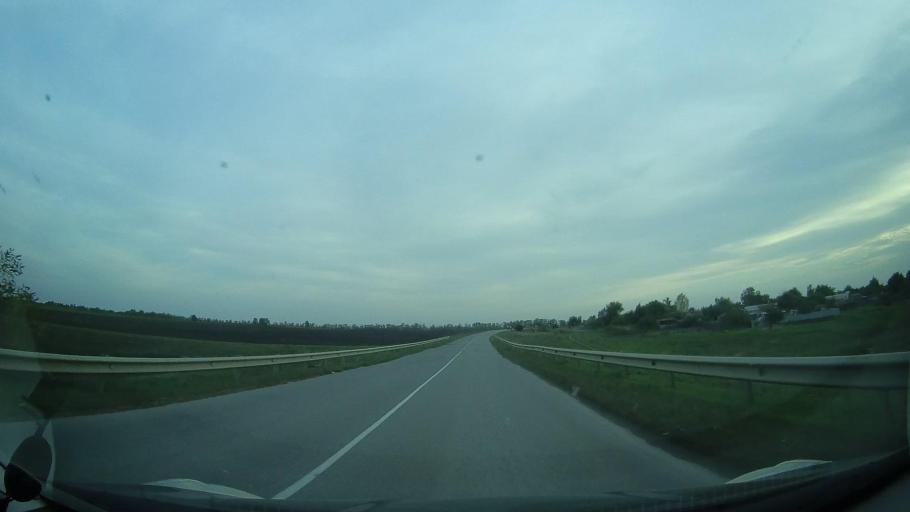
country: RU
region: Rostov
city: Kirovskaya
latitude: 47.0339
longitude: 39.9811
